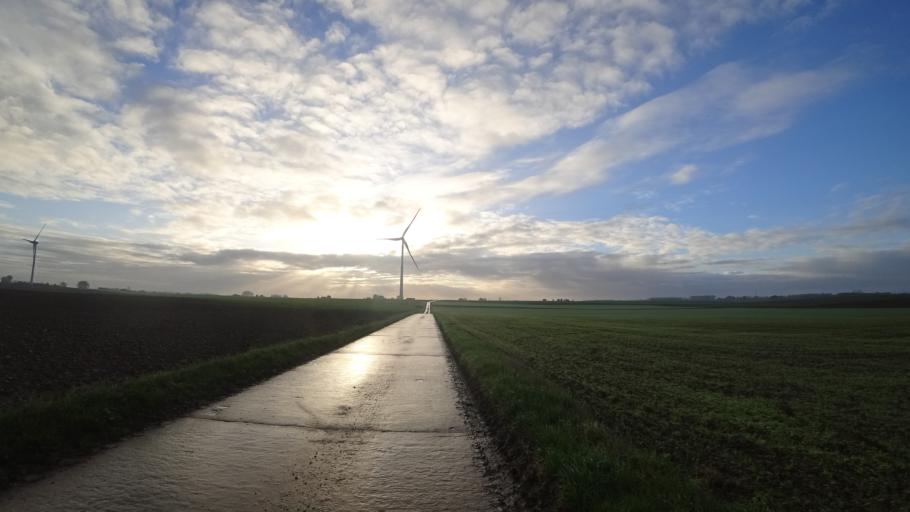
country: BE
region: Wallonia
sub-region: Province du Brabant Wallon
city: Walhain-Saint-Paul
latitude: 50.5943
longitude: 4.6874
